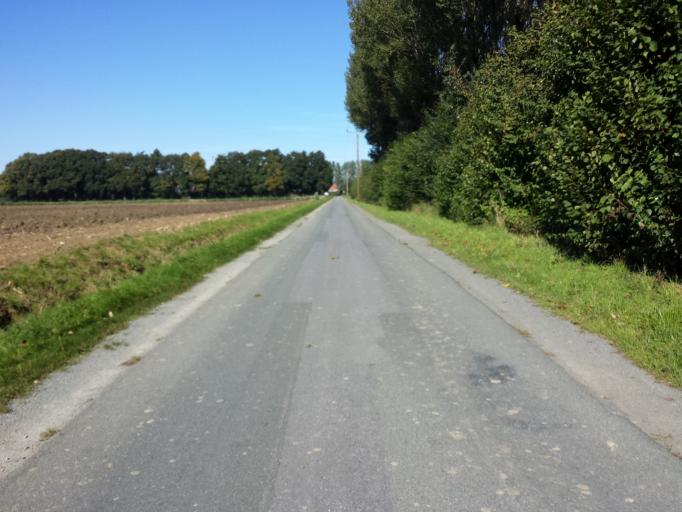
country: DE
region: North Rhine-Westphalia
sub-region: Regierungsbezirk Detmold
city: Langenberg
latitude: 51.7832
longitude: 8.3368
